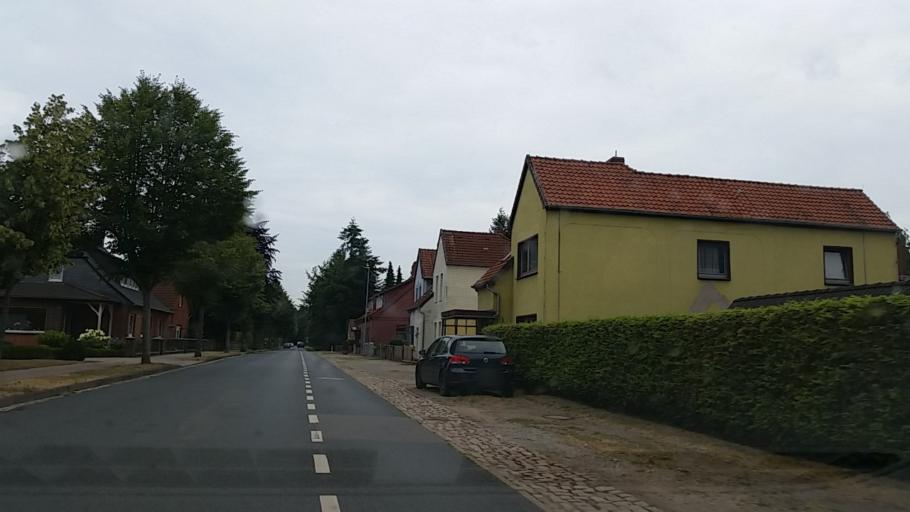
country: DE
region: Lower Saxony
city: Schwarmstedt
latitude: 52.6925
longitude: 9.6032
